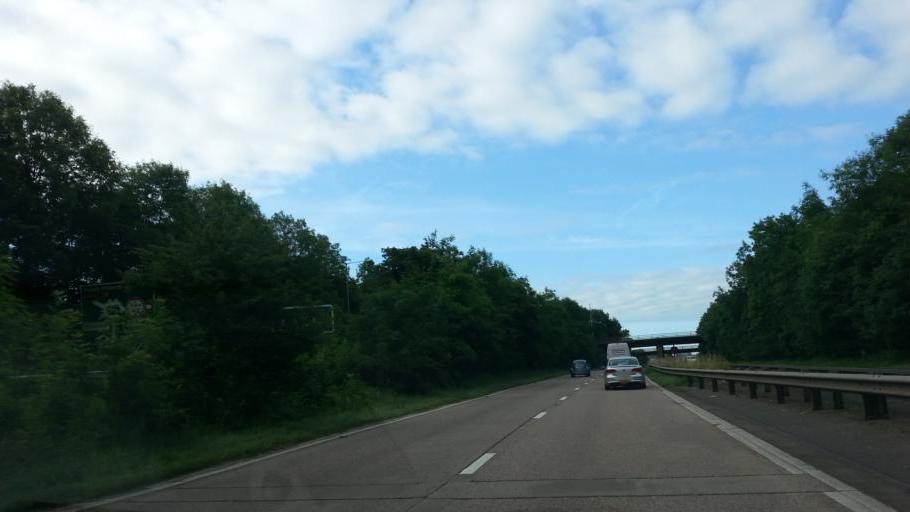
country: GB
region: England
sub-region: Nottinghamshire
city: Cotgrave
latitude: 52.8545
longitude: -1.0313
